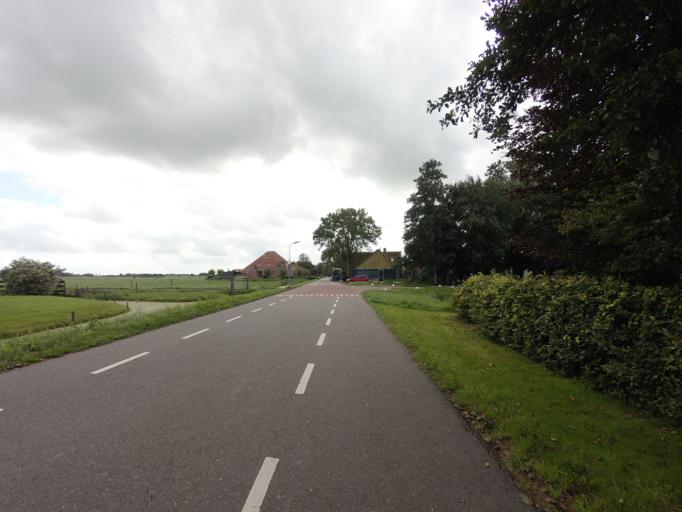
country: NL
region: North Holland
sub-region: Gemeente Edam-Volendam
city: Edam
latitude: 52.5384
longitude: 5.0141
